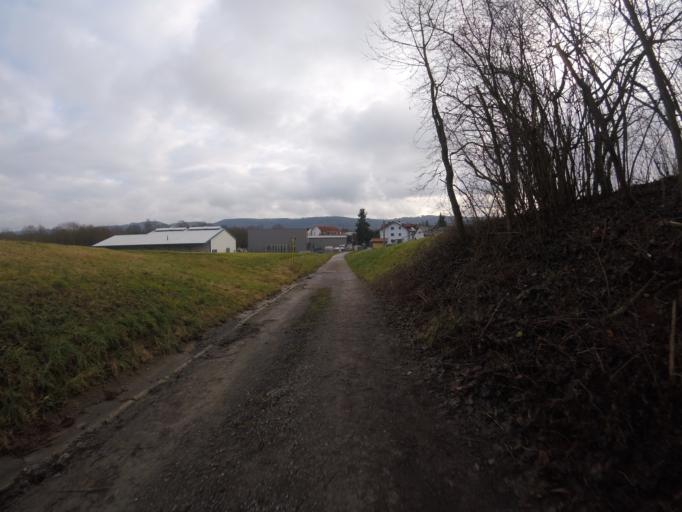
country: DE
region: Baden-Wuerttemberg
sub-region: Regierungsbezirk Stuttgart
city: Allmersbach im Tal
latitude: 48.9223
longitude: 9.4820
